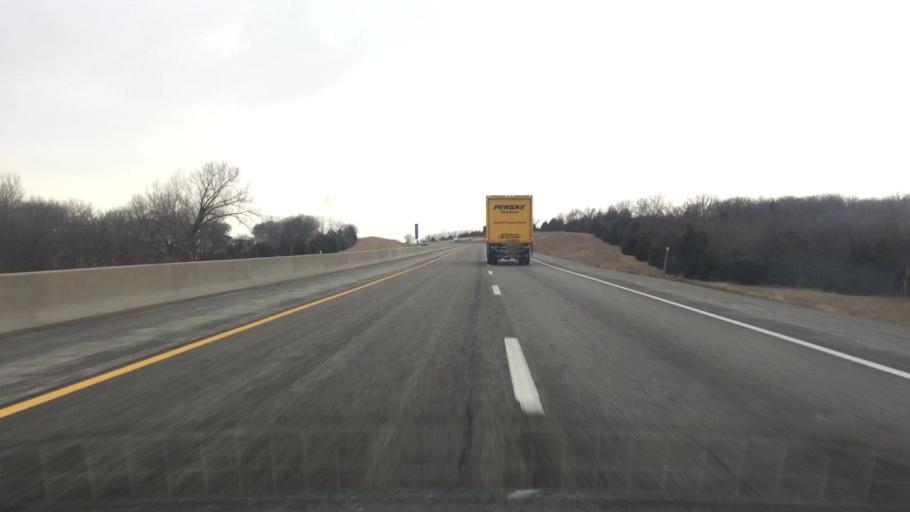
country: US
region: Kansas
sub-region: Shawnee County
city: Topeka
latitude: 38.9609
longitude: -95.7264
